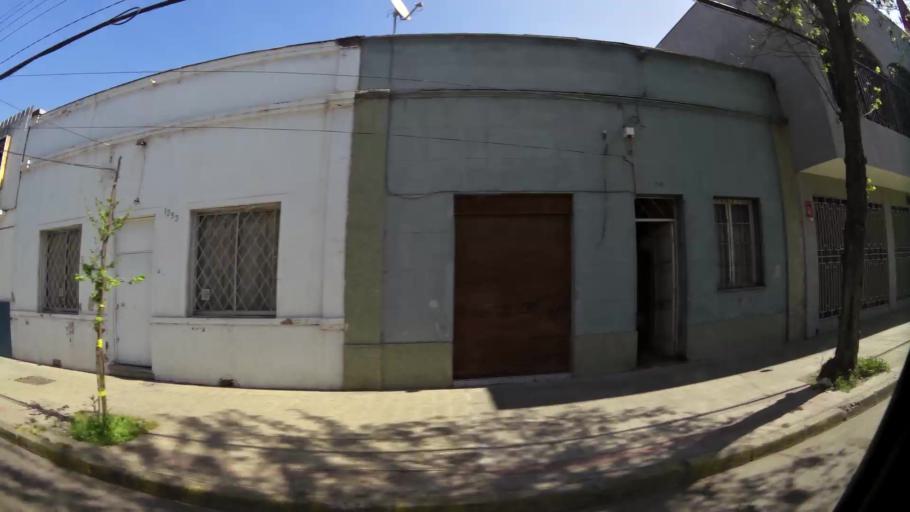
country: CL
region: Santiago Metropolitan
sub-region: Provincia de Santiago
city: Santiago
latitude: -33.4605
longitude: -70.6335
